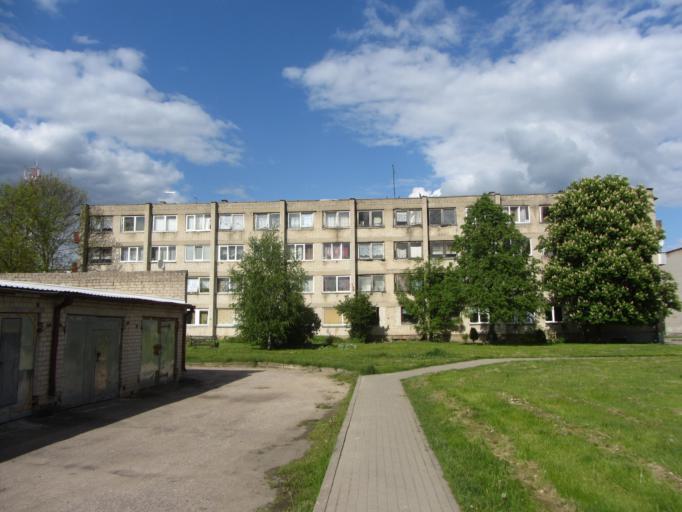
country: LT
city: Sirvintos
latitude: 55.0415
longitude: 24.9552
